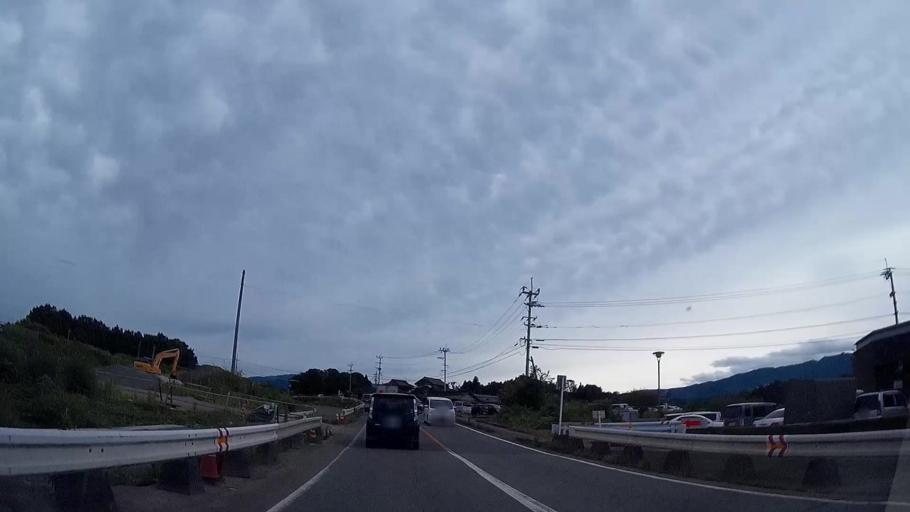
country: JP
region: Kumamoto
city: Kikuchi
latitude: 32.9477
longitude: 130.8233
